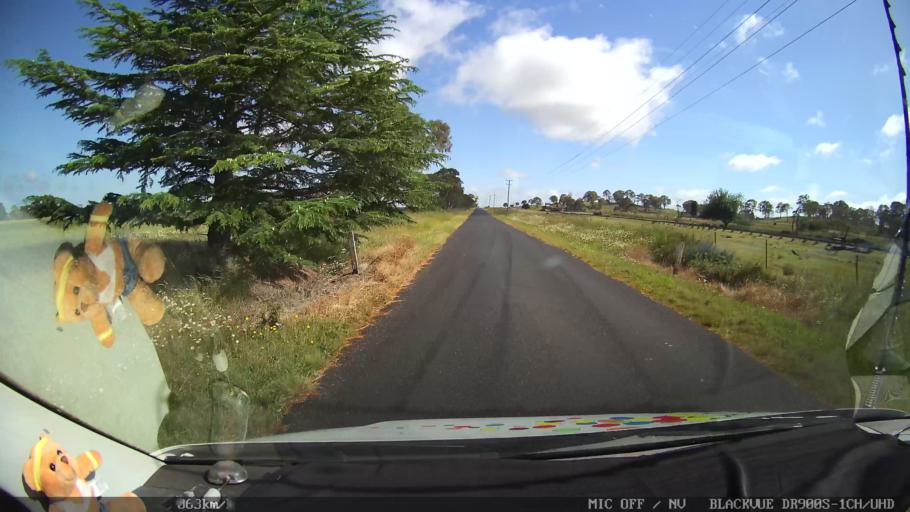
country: AU
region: New South Wales
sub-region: Guyra
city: Guyra
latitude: -30.2013
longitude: 151.6750
